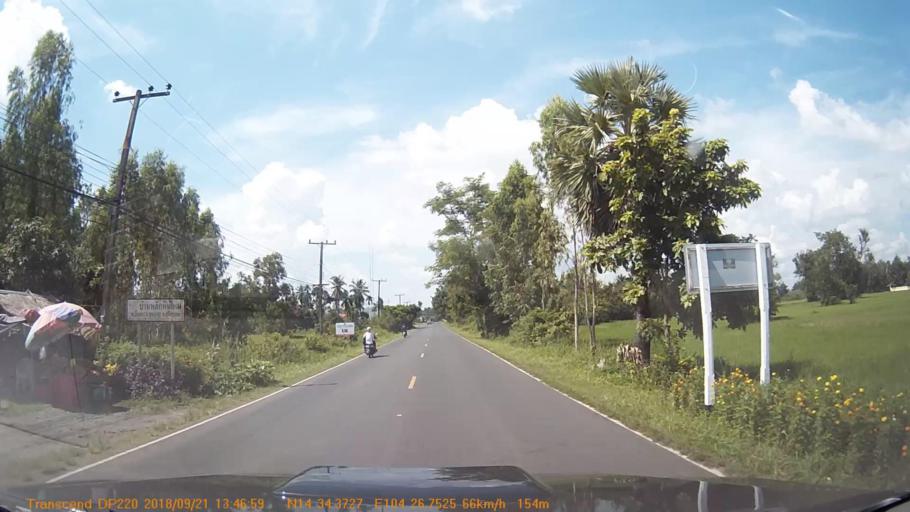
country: TH
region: Sisaket
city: Khun Han
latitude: 14.5732
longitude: 104.4458
